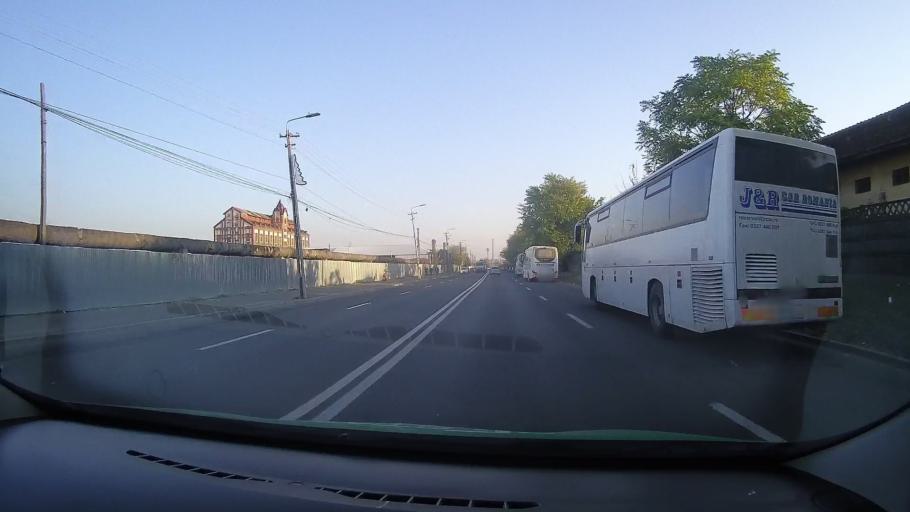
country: RO
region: Arad
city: Arad
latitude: 46.1924
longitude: 21.3198
